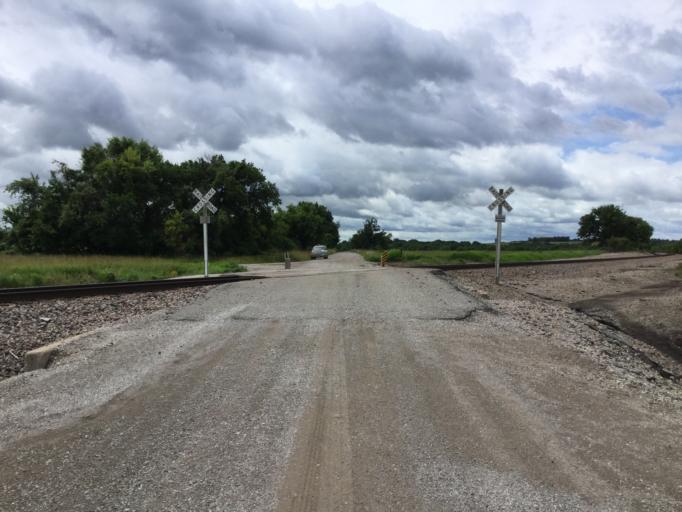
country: US
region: Kansas
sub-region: Bourbon County
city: Fort Scott
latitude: 37.6997
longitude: -94.7956
